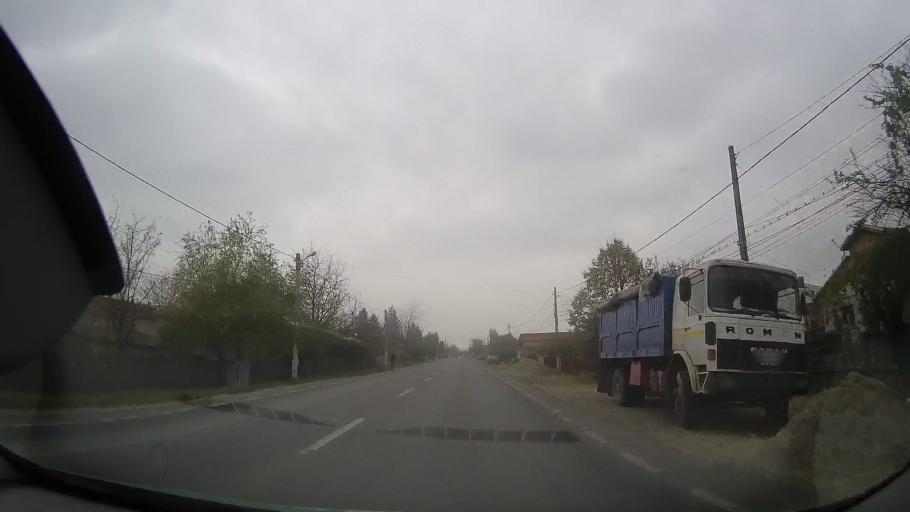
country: RO
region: Ialomita
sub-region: Comuna Manasia
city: Manasia
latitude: 44.7100
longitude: 26.6642
